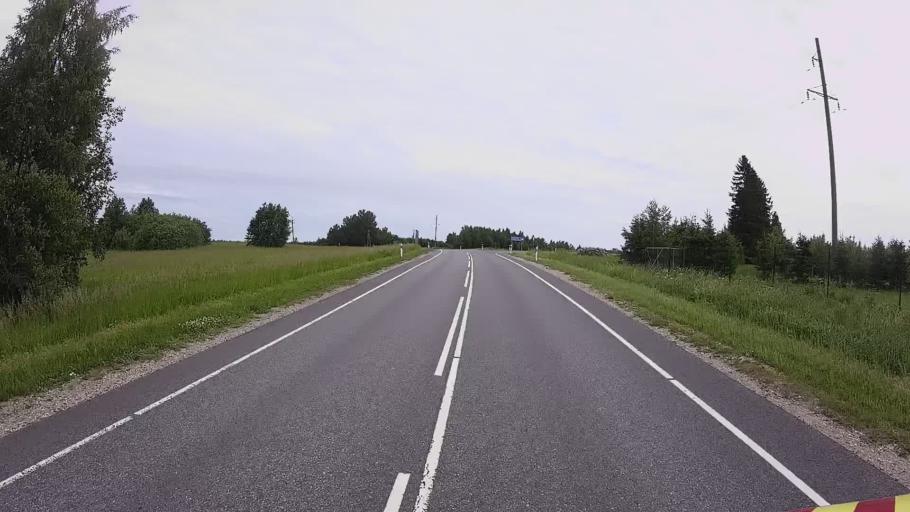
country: EE
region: Viljandimaa
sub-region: Karksi vald
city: Karksi-Nuia
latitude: 58.1500
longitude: 25.5957
